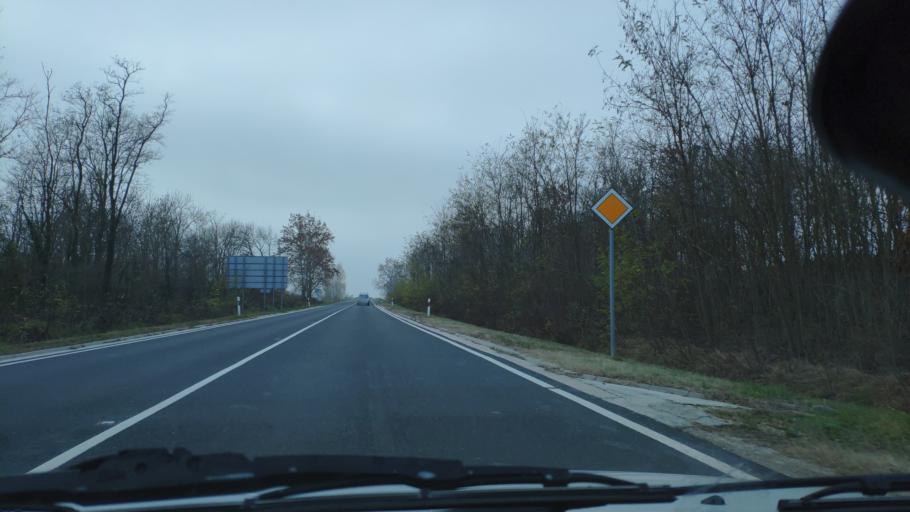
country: HU
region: Zala
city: Zalakomar
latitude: 46.5336
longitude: 17.2011
